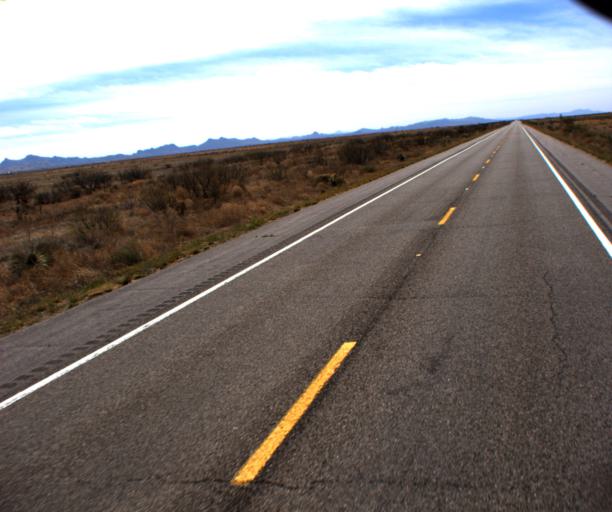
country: US
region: Arizona
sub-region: Cochise County
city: Pirtleville
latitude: 31.5335
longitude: -109.6530
